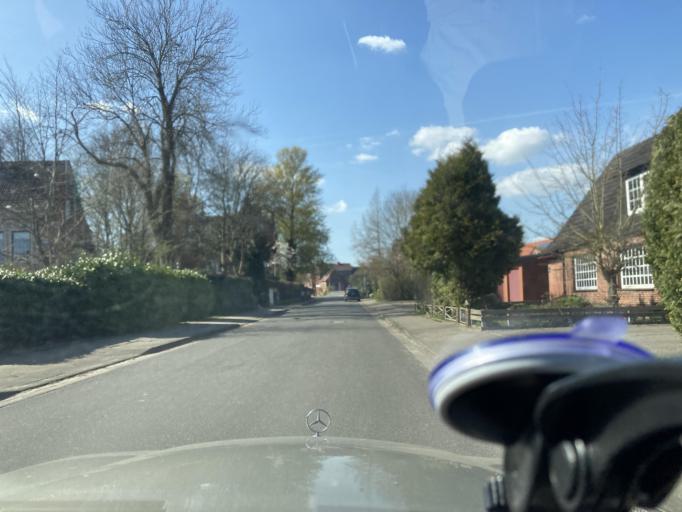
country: DE
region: Schleswig-Holstein
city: Friedrichstadt
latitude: 54.3747
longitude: 9.0930
